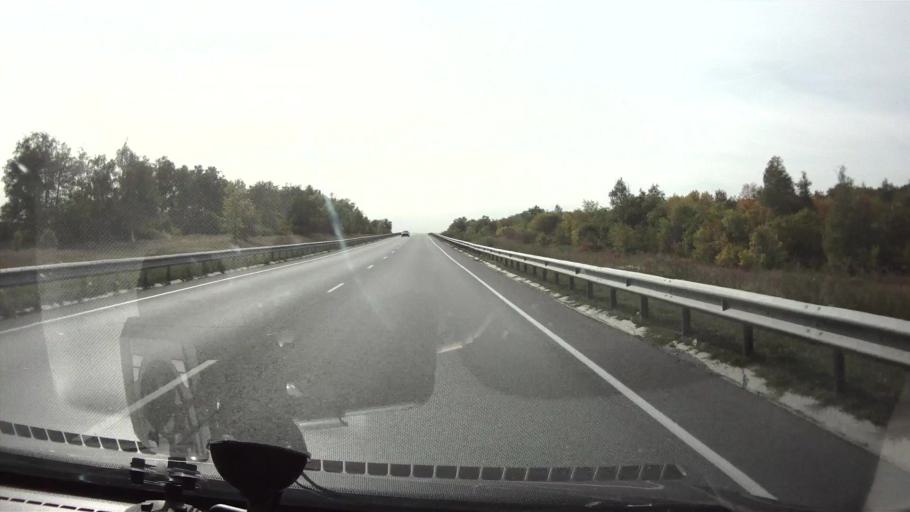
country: RU
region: Saratov
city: Balakovo
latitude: 52.0910
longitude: 47.6962
